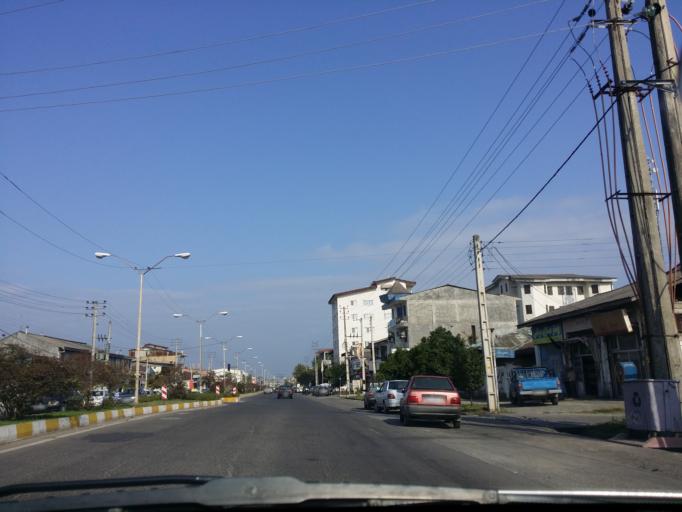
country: IR
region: Mazandaran
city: Chalus
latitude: 36.6714
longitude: 51.4073
